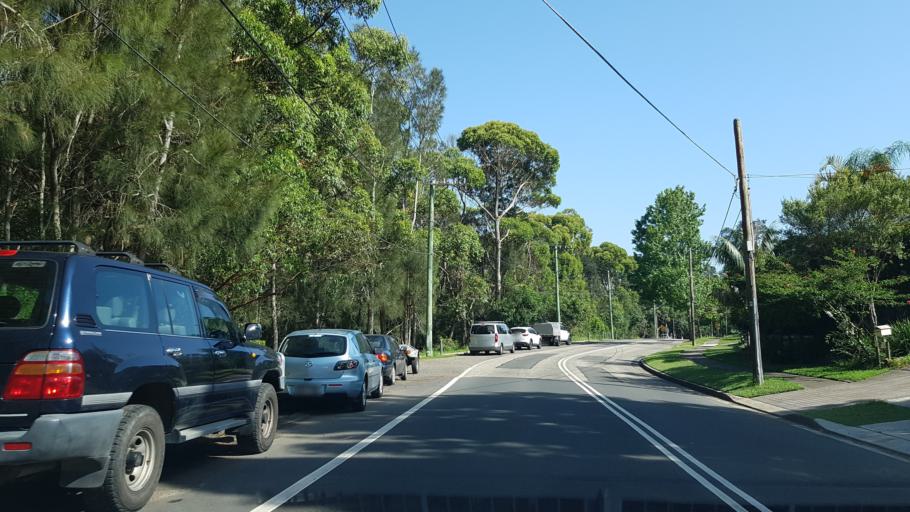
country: AU
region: New South Wales
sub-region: Warringah
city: Narraweena
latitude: -33.7309
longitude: 151.2769
